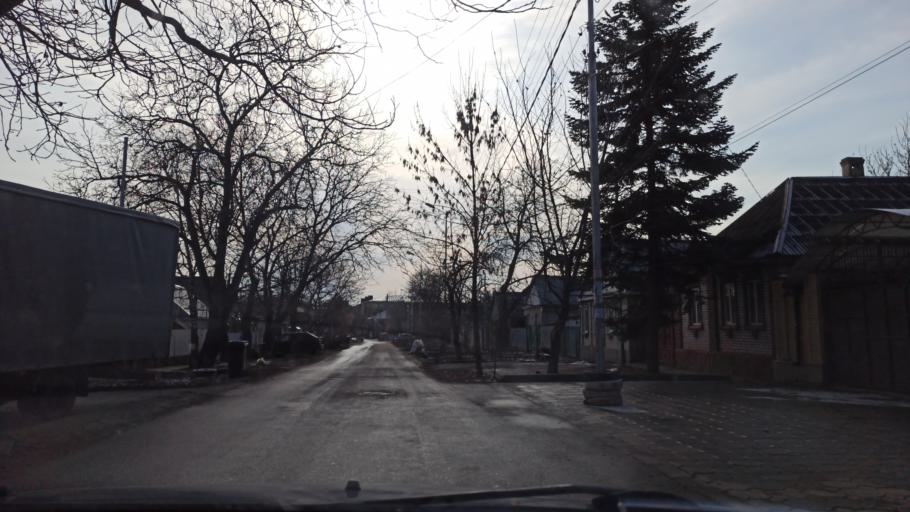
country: RU
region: Stavropol'skiy
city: Yessentukskaya
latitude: 44.0410
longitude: 42.8798
